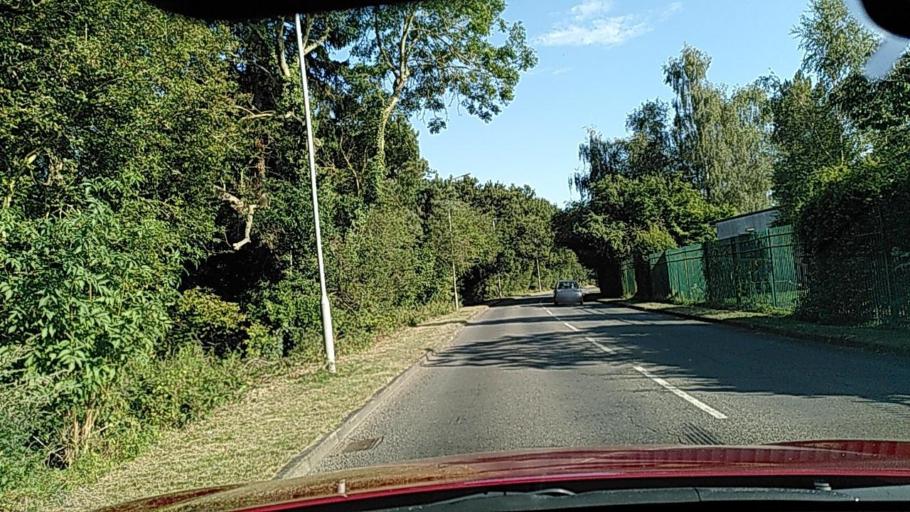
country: GB
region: England
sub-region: Reading
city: Reading
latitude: 51.4854
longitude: -0.9484
